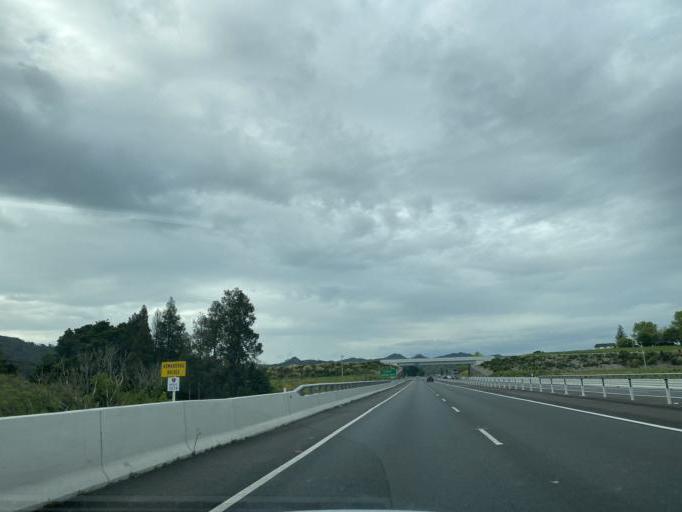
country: NZ
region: Waikato
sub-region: Waikato District
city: Ngaruawahia
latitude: -37.6144
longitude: 175.2047
